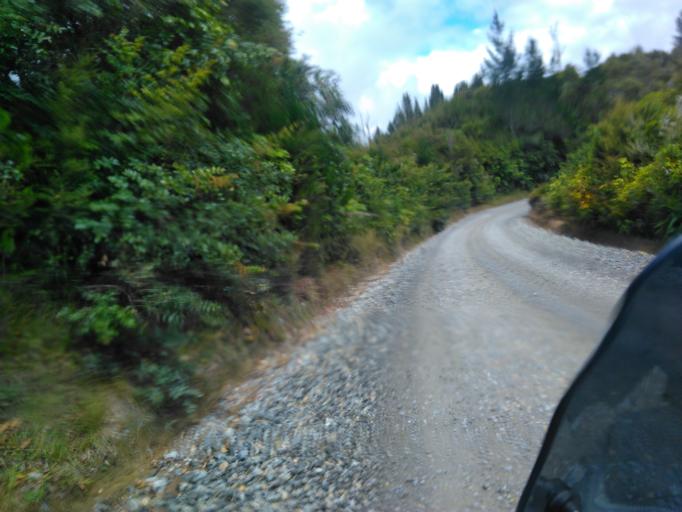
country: NZ
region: Gisborne
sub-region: Gisborne District
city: Gisborne
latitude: -38.2364
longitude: 178.0676
